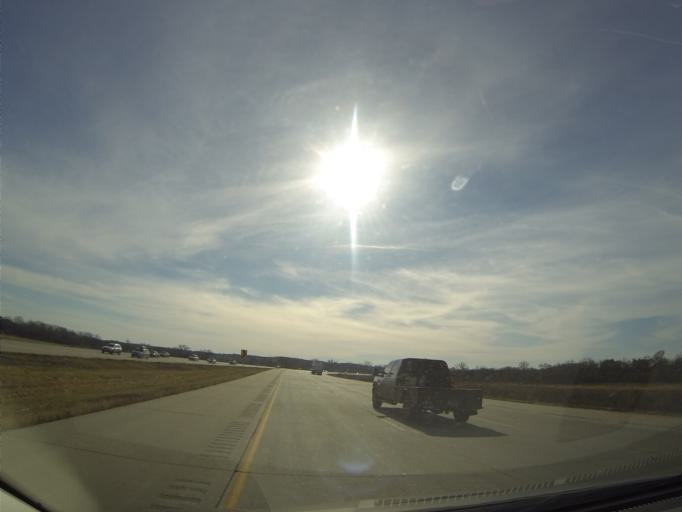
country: US
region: Nebraska
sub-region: Saunders County
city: Ashland
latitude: 41.0380
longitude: -96.2923
